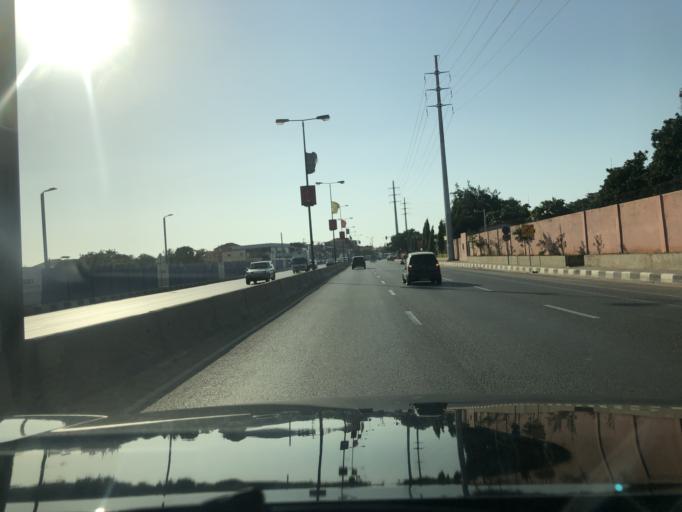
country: AO
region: Luanda
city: Luanda
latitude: -8.9057
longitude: 13.1784
